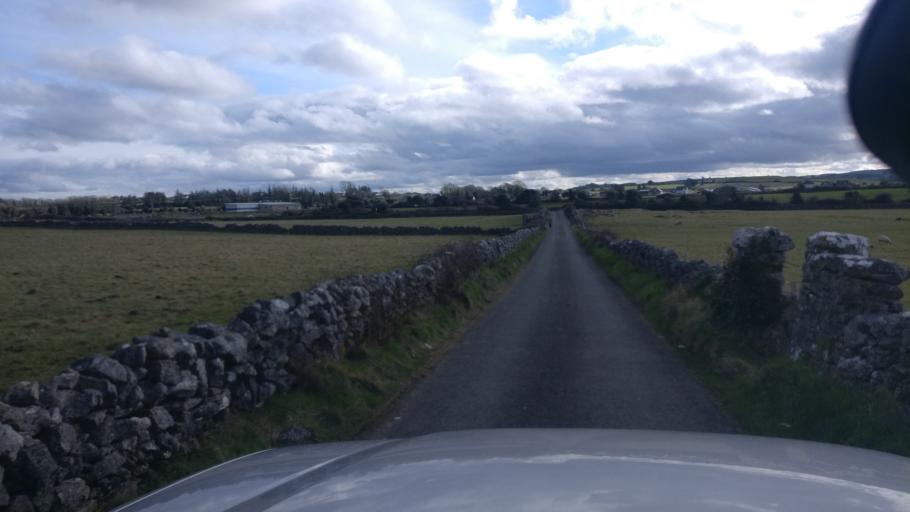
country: IE
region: Connaught
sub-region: County Galway
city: Loughrea
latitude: 53.1986
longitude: -8.5423
